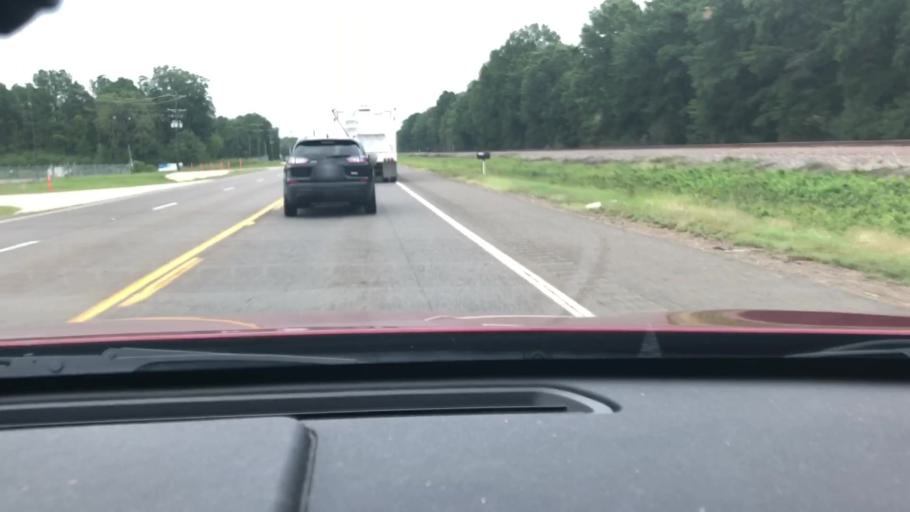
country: US
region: Arkansas
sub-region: Lafayette County
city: Lewisville
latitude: 33.3581
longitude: -93.6049
